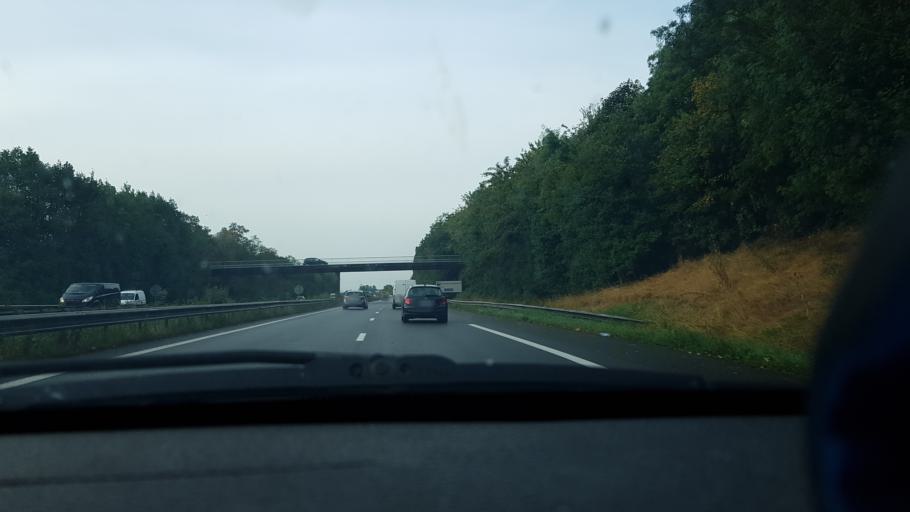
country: FR
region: Lorraine
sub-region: Departement de Meurthe-et-Moselle
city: Vandoeuvre-les-Nancy
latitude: 48.6469
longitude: 6.1812
